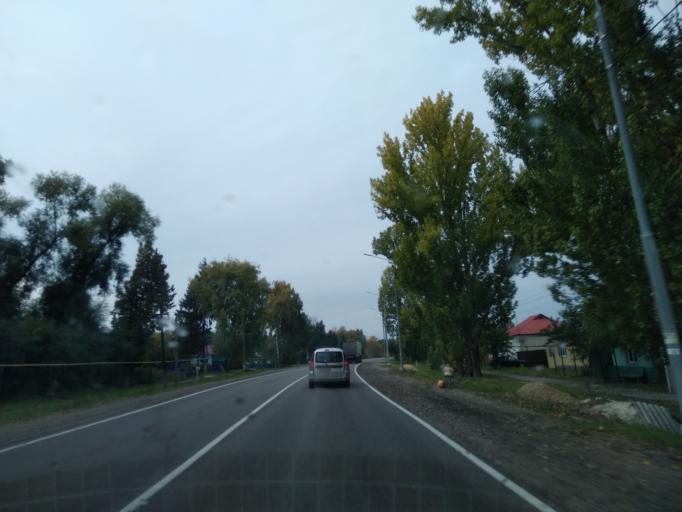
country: RU
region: Lipetsk
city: Zadonsk
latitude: 52.4176
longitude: 38.8518
